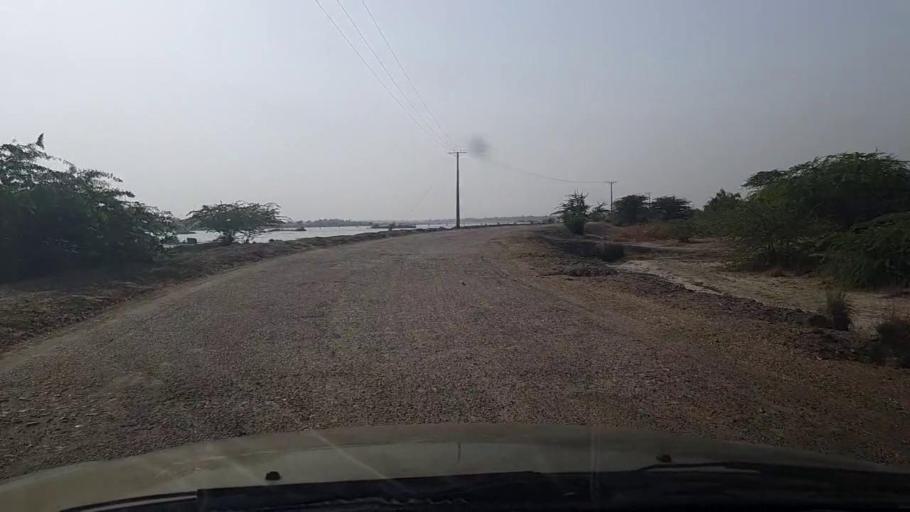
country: PK
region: Sindh
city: Kot Diji
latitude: 27.2957
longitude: 68.6431
